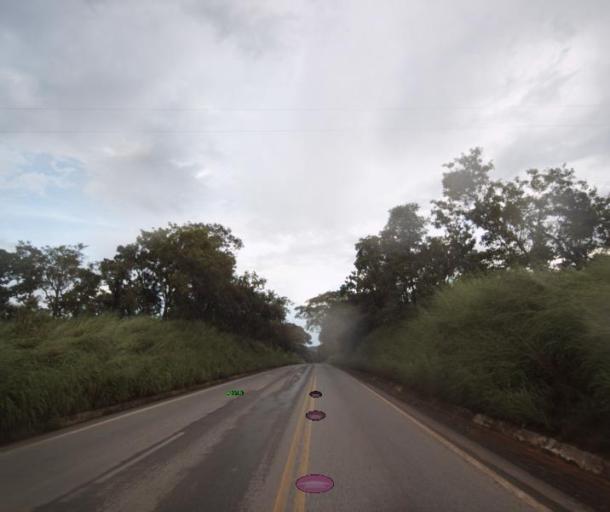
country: BR
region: Goias
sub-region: Porangatu
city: Porangatu
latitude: -13.9241
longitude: -49.0700
